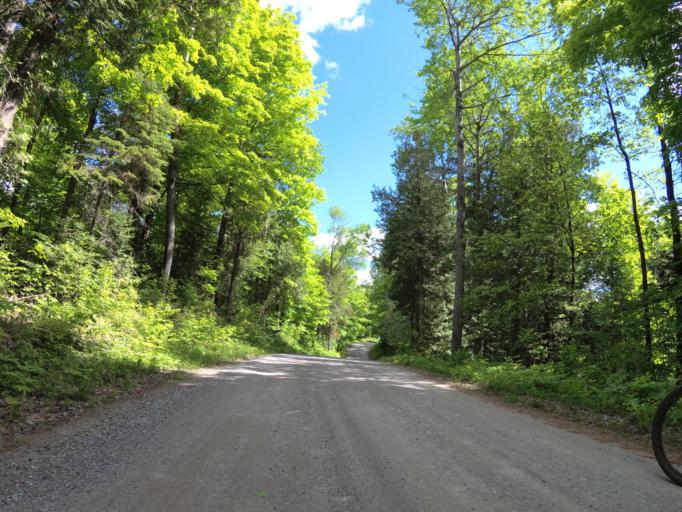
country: CA
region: Ontario
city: Renfrew
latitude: 45.0444
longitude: -76.8243
